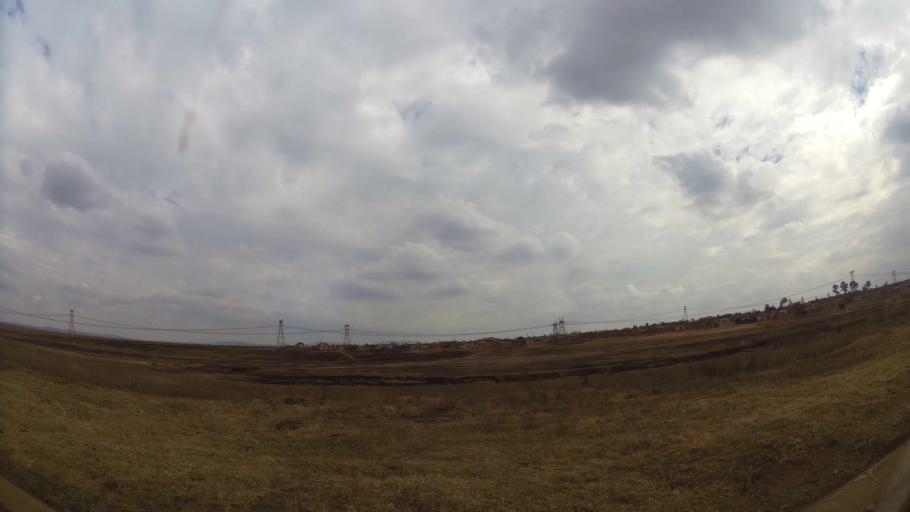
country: ZA
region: Gauteng
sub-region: Ekurhuleni Metropolitan Municipality
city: Germiston
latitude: -26.3809
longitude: 28.1156
